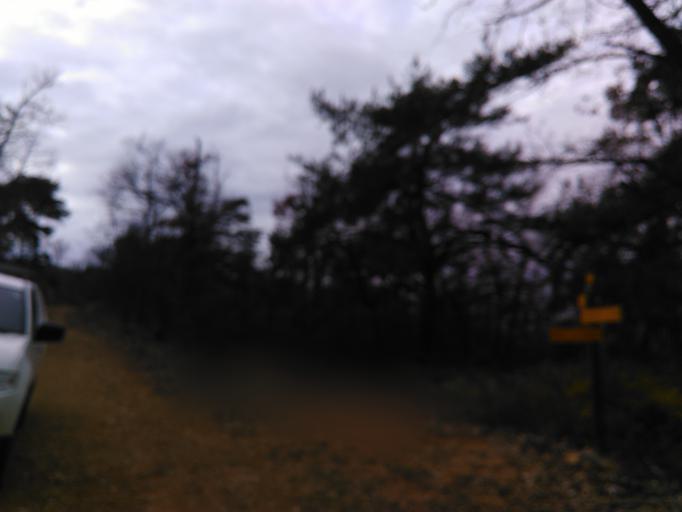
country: FR
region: Rhone-Alpes
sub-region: Departement de la Drome
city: Nyons
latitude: 44.3064
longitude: 5.1719
